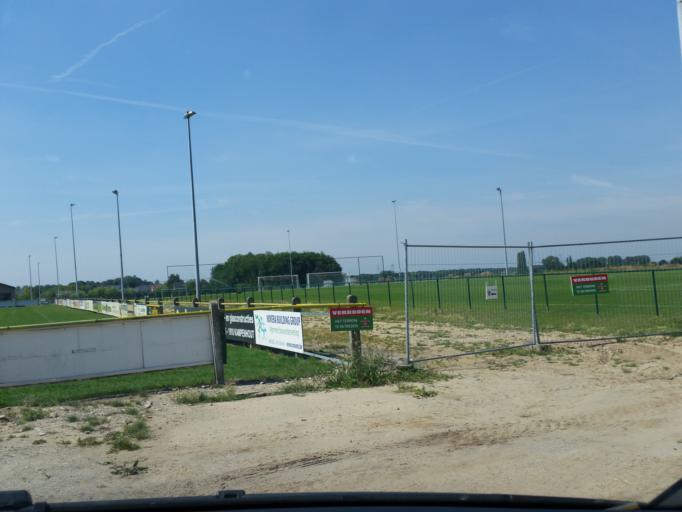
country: BE
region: Flanders
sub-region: Provincie Vlaams-Brabant
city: Zemst
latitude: 50.9719
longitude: 4.4505
